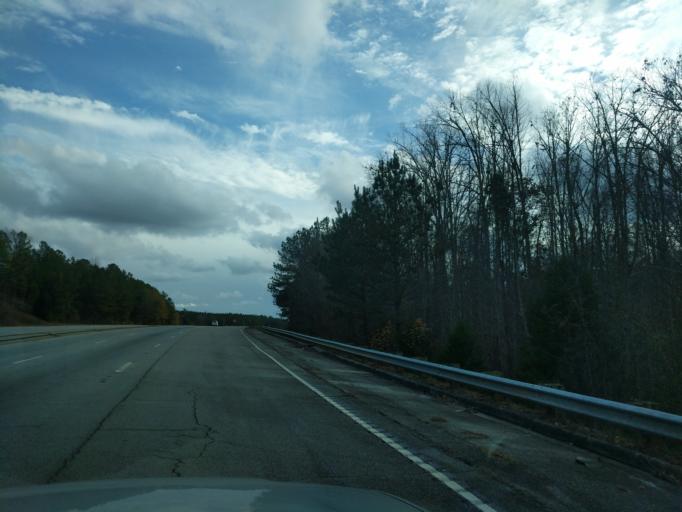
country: US
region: South Carolina
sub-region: Greenwood County
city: Ware Shoals
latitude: 34.4061
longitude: -82.2248
